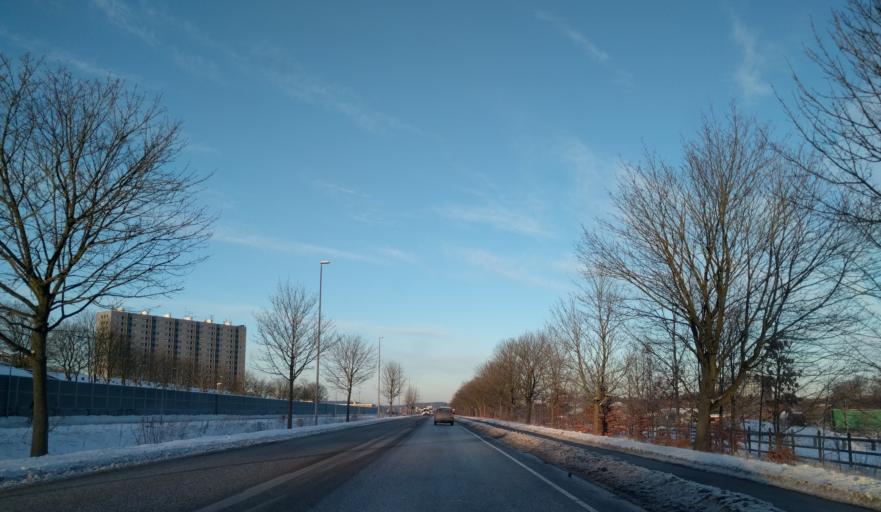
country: DK
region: North Denmark
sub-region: Alborg Kommune
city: Aalborg
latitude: 57.0223
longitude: 9.9490
